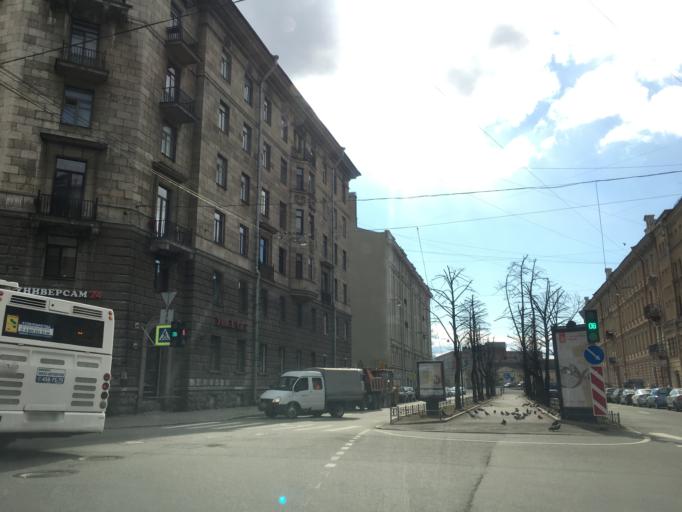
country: RU
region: St.-Petersburg
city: Admiralteisky
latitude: 59.9239
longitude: 30.2843
